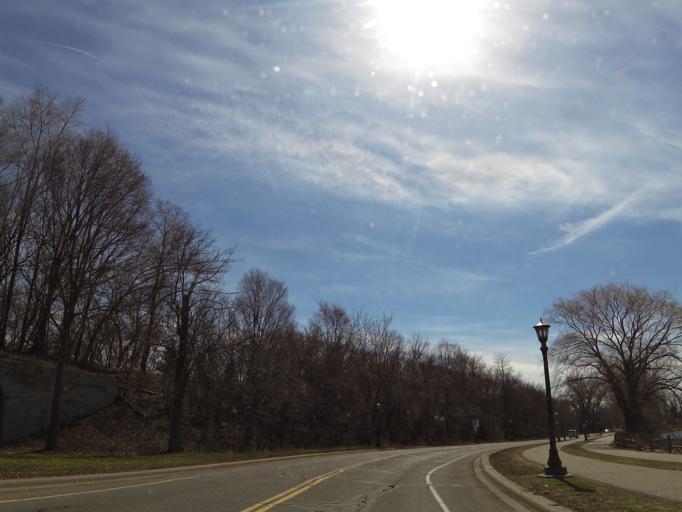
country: US
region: Minnesota
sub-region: Ramsey County
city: Maplewood
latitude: 44.9830
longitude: -93.0459
